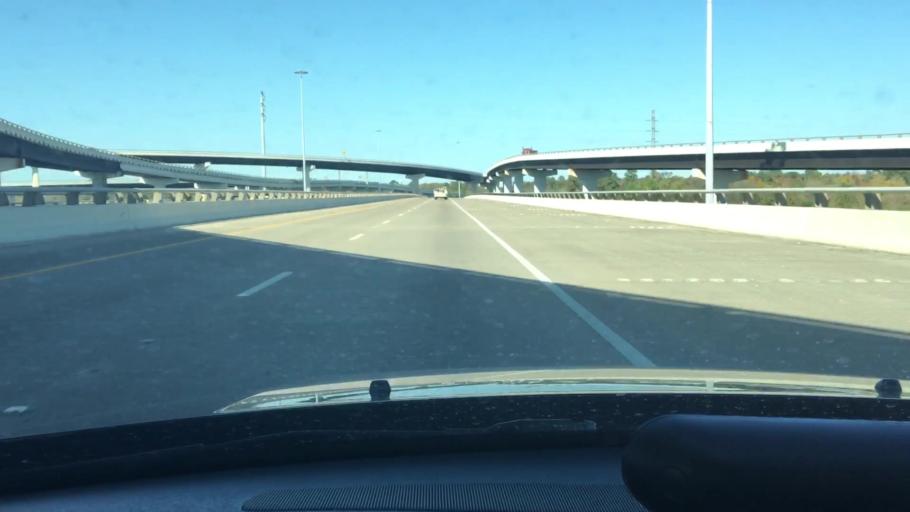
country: US
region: Texas
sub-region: Harris County
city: Cloverleaf
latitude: 29.7713
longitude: -95.1536
